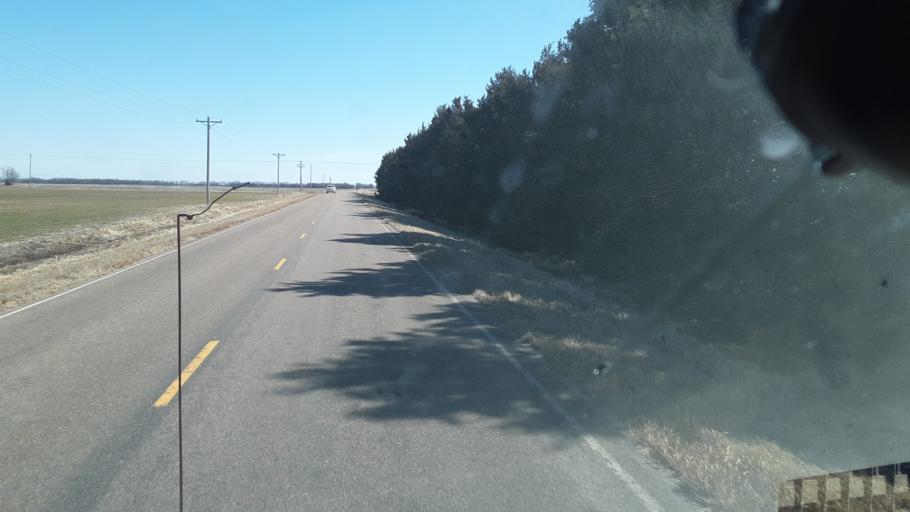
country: US
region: Kansas
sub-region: Rice County
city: Sterling
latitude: 38.2462
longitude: -98.2552
